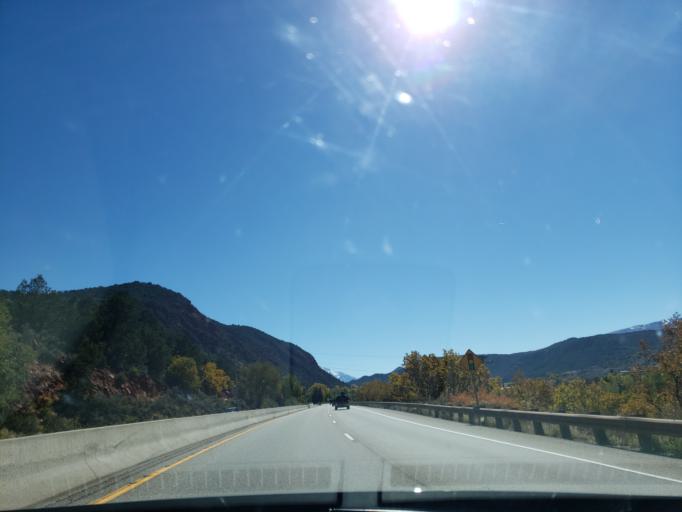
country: US
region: Colorado
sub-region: Garfield County
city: Glenwood Springs
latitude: 39.5093
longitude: -107.3052
